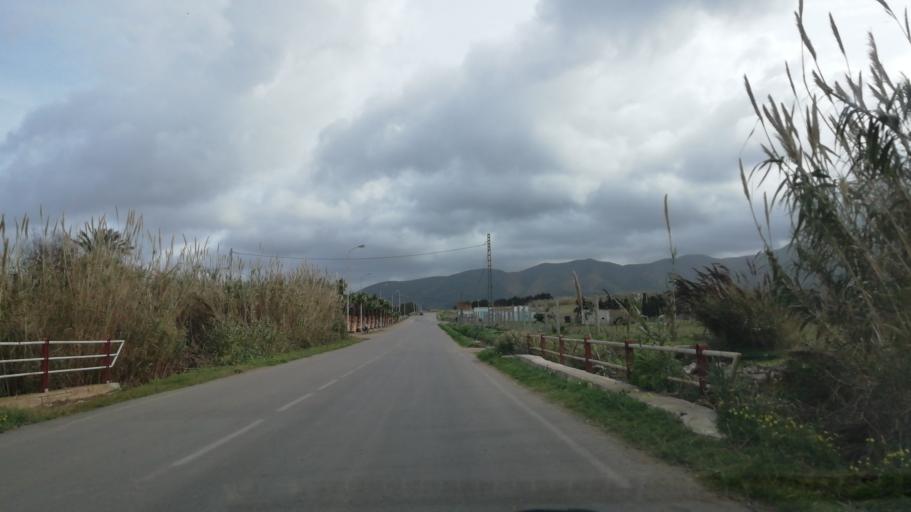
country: DZ
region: Oran
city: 'Ain el Turk
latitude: 35.7005
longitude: -0.8864
